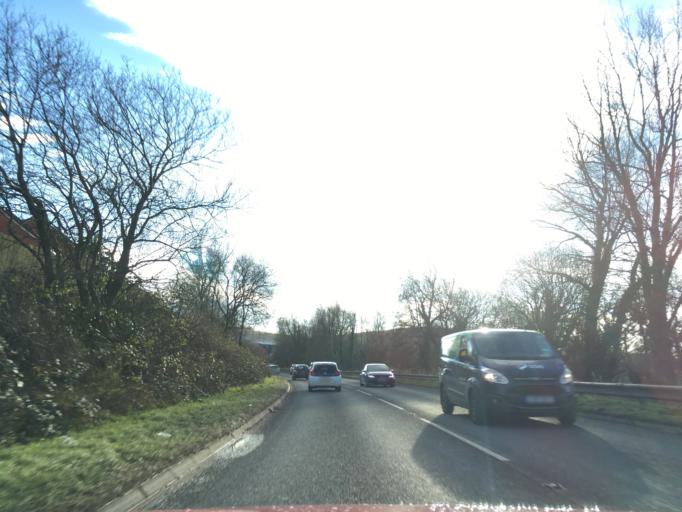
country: GB
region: Wales
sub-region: Caerphilly County Borough
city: Caerphilly
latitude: 51.5746
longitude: -3.2471
